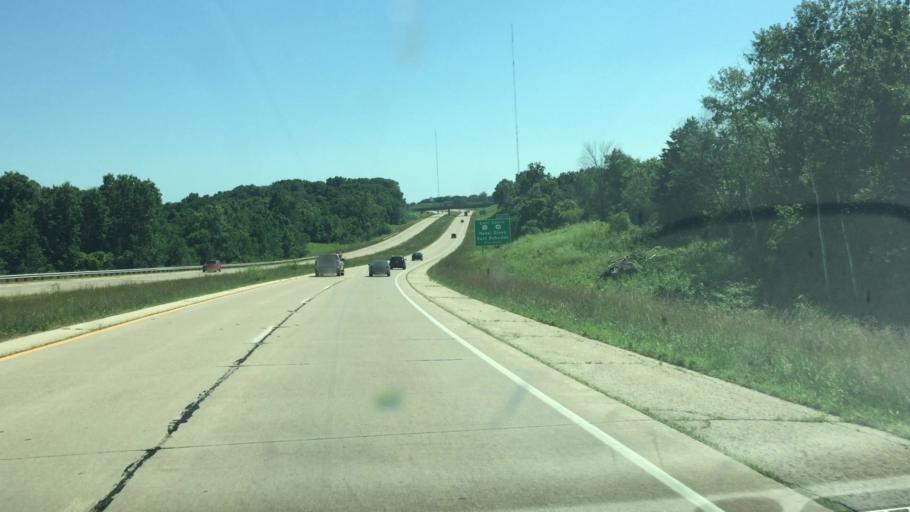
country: US
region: Illinois
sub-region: Jo Daviess County
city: East Dubuque
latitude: 42.5415
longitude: -90.6079
